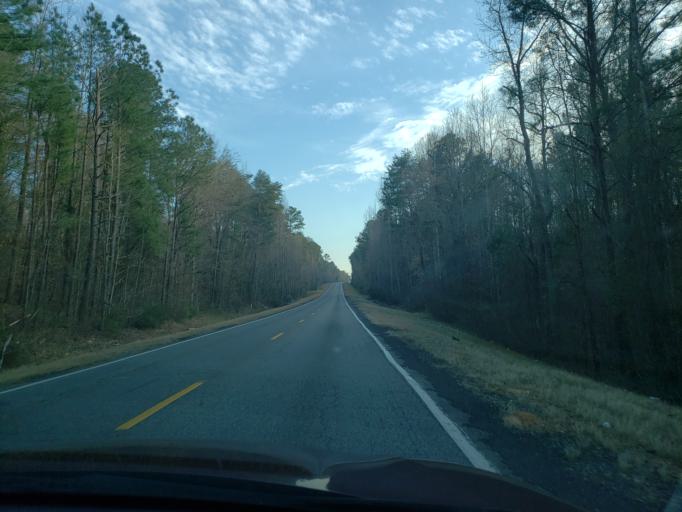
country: US
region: Alabama
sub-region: Hale County
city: Greensboro
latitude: 32.7513
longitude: -87.5852
